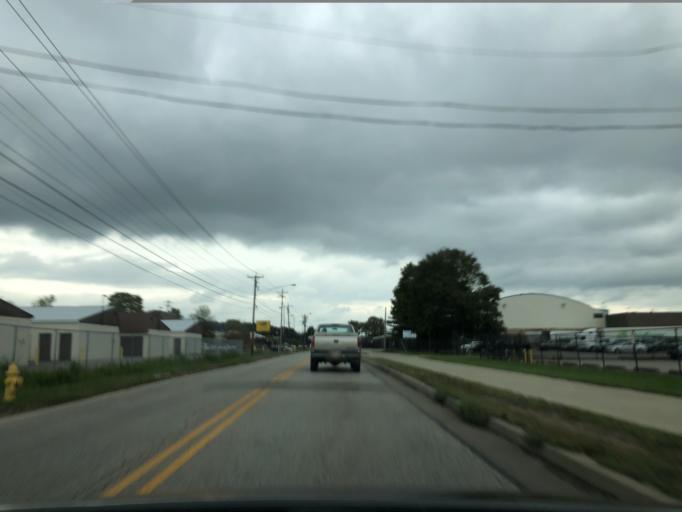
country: US
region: Ohio
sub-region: Hamilton County
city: Turpin Hills
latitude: 39.1095
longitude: -84.4209
